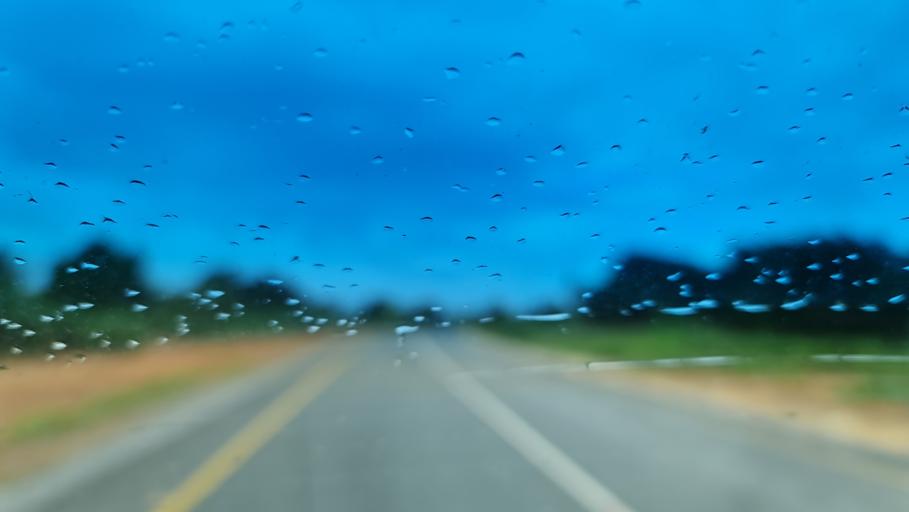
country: MZ
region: Nampula
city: Nampula
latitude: -15.5339
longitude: 39.3309
